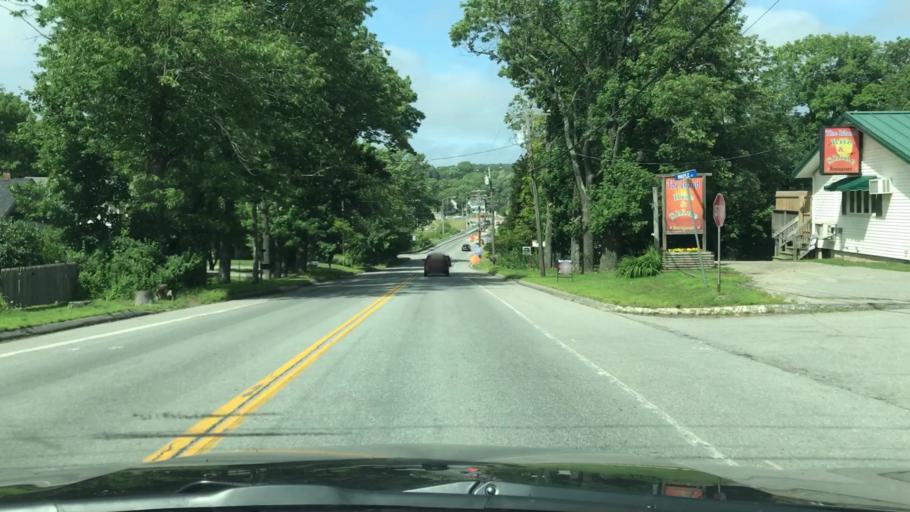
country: US
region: Maine
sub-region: Hancock County
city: Bucksport
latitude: 44.5662
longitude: -68.7901
